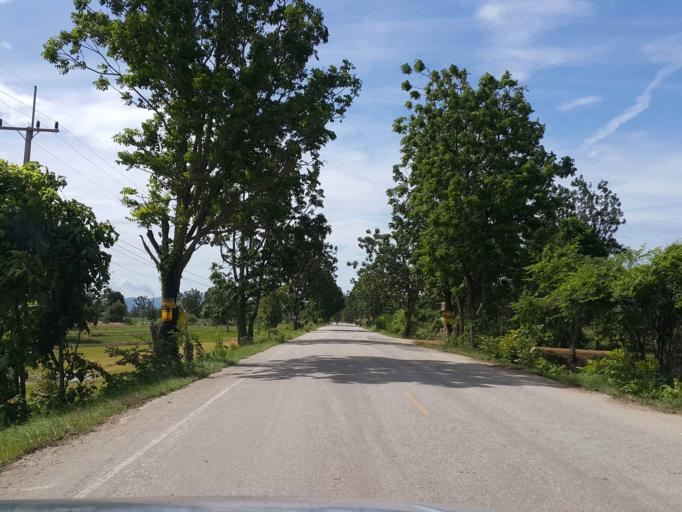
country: TH
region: Sukhothai
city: Ban Dan Lan Hoi
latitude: 17.1402
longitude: 99.5239
